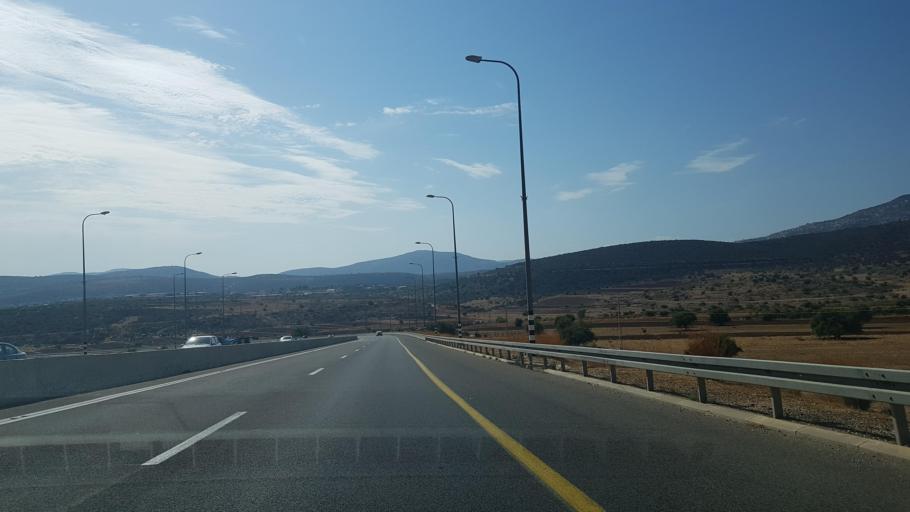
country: IL
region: Northern District
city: Maghar
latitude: 32.8865
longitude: 35.4768
